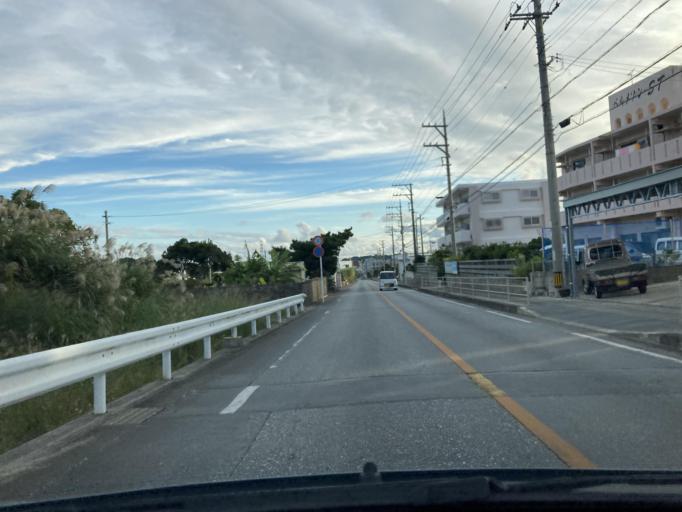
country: JP
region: Okinawa
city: Itoman
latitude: 26.1425
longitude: 127.6889
